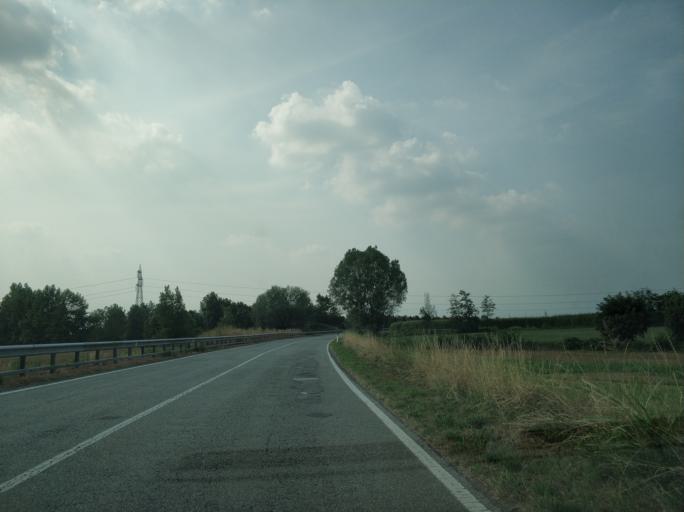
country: IT
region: Piedmont
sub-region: Provincia di Torino
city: Borgaro Torinese
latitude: 45.1418
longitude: 7.6812
